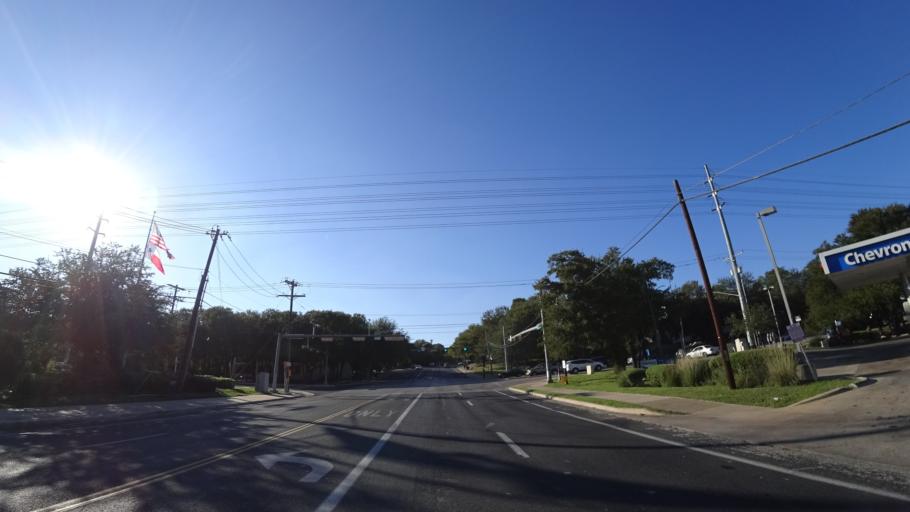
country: US
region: Texas
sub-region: Travis County
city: Austin
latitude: 30.2273
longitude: -97.7272
